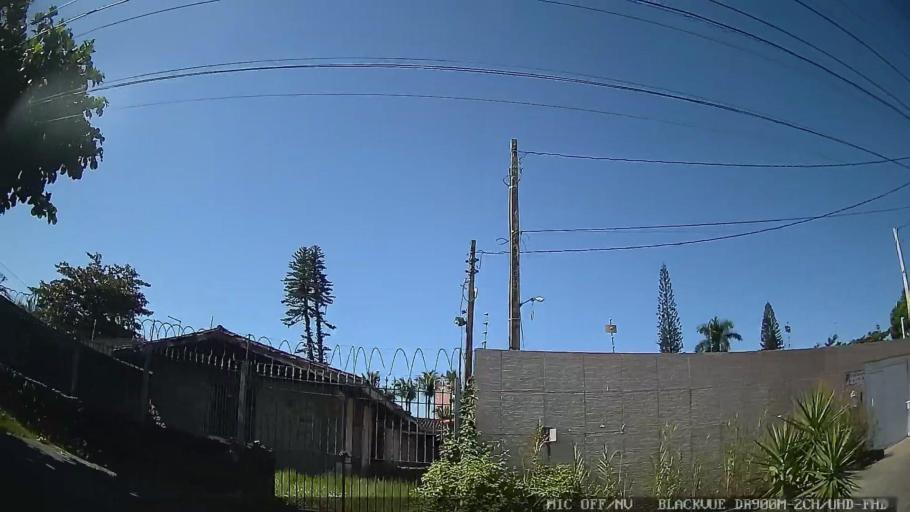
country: BR
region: Sao Paulo
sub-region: Guaruja
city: Guaruja
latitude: -23.9803
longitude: -46.2130
